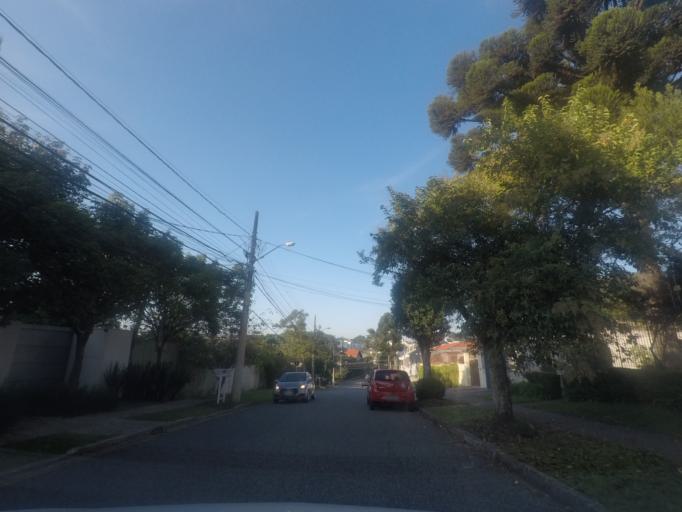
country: BR
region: Parana
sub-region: Curitiba
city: Curitiba
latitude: -25.4065
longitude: -49.2727
